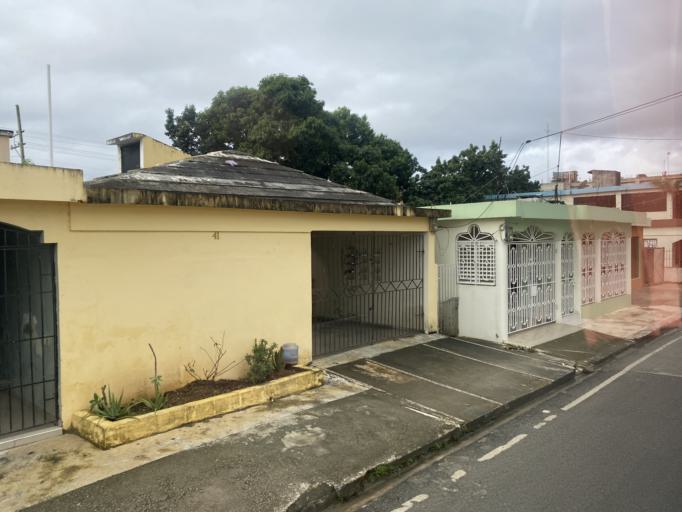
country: DO
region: El Seibo
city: Miches
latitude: 18.9842
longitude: -69.0456
